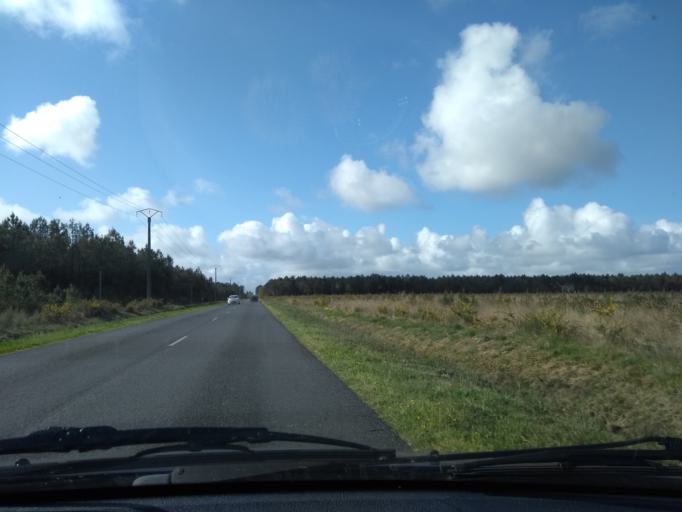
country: FR
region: Aquitaine
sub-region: Departement des Landes
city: Parentis-en-Born
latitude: 44.3700
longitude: -1.0739
